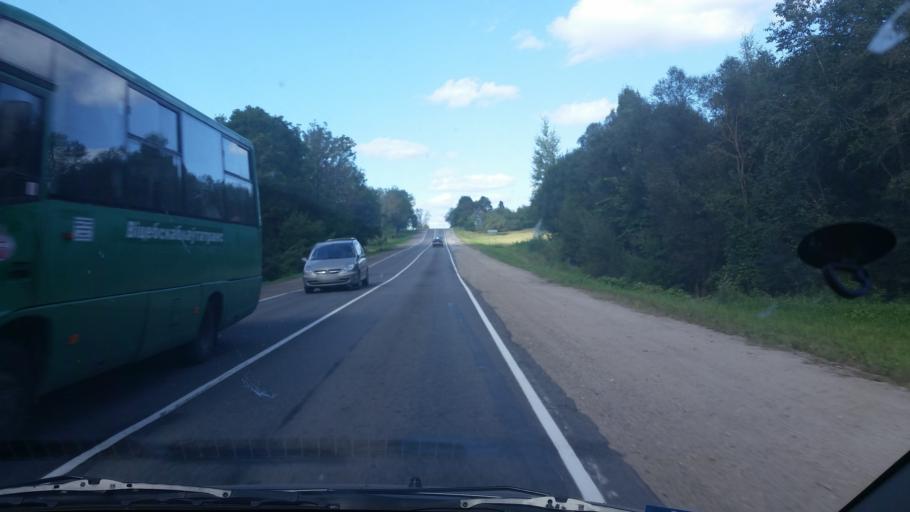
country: BY
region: Vitebsk
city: Vitebsk
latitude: 55.1082
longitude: 30.2835
